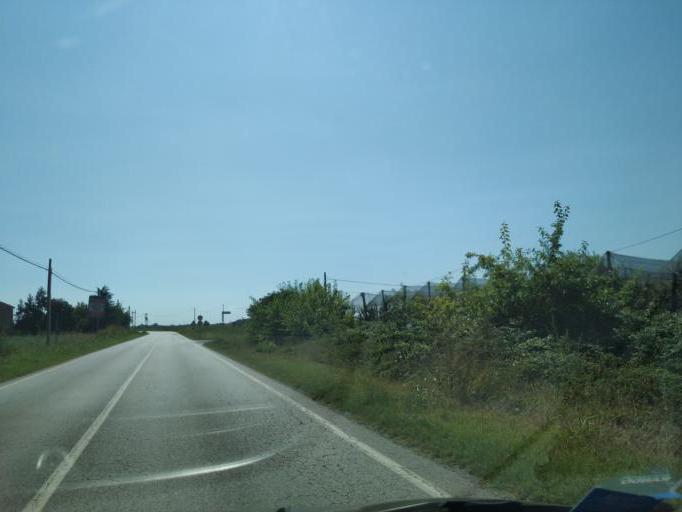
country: IT
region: Emilia-Romagna
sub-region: Provincia di Ferrara
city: Copparo
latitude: 44.8887
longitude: 11.8480
